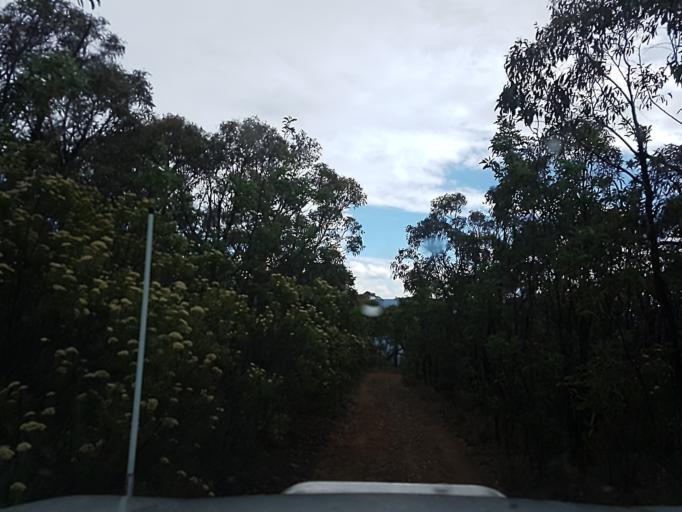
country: AU
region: New South Wales
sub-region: Snowy River
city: Jindabyne
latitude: -36.9114
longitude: 148.3355
